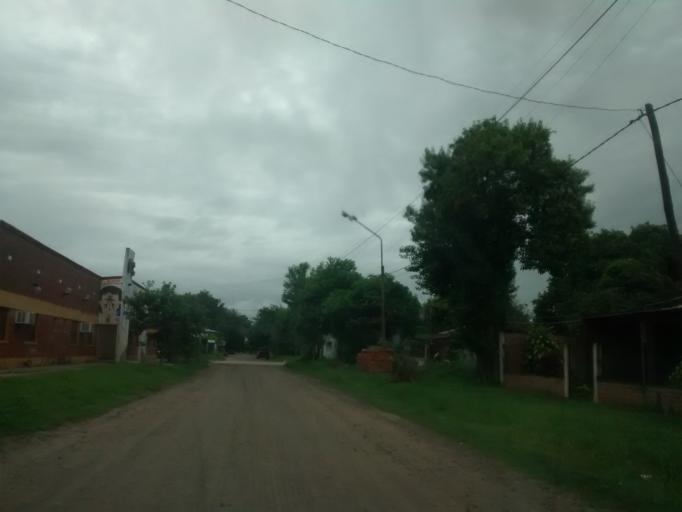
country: AR
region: Chaco
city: Puerto Tirol
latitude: -27.3736
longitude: -59.0966
